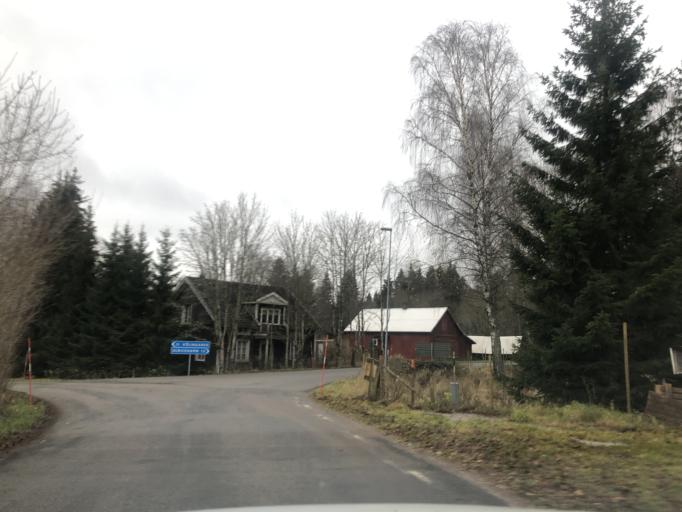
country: SE
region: Vaestra Goetaland
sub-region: Ulricehamns Kommun
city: Ulricehamn
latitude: 57.8773
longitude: 13.5299
